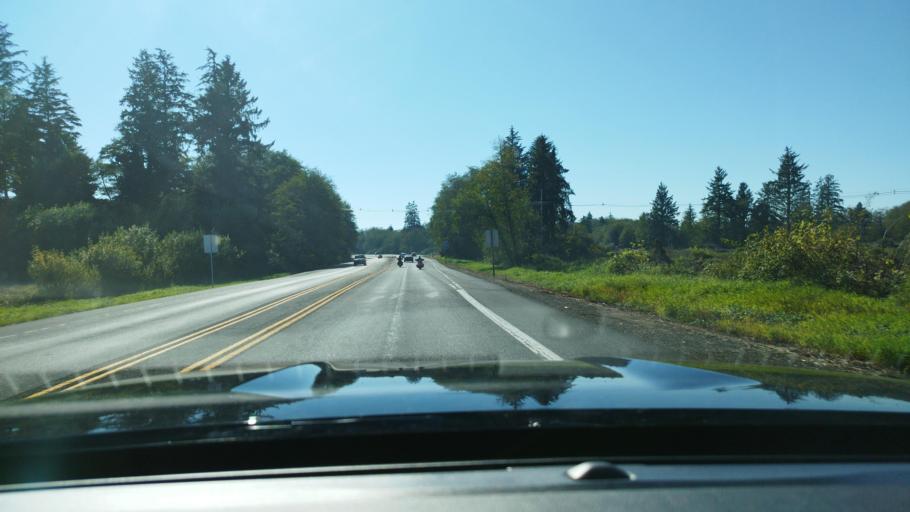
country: US
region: Oregon
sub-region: Clatsop County
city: Warrenton
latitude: 46.1550
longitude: -123.9088
